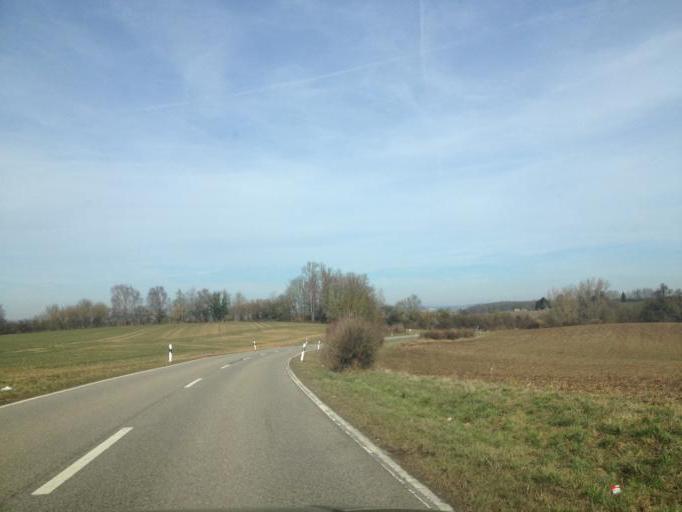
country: DE
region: Baden-Wuerttemberg
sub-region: Regierungsbezirk Stuttgart
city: Oedheim
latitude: 49.2141
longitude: 9.2744
